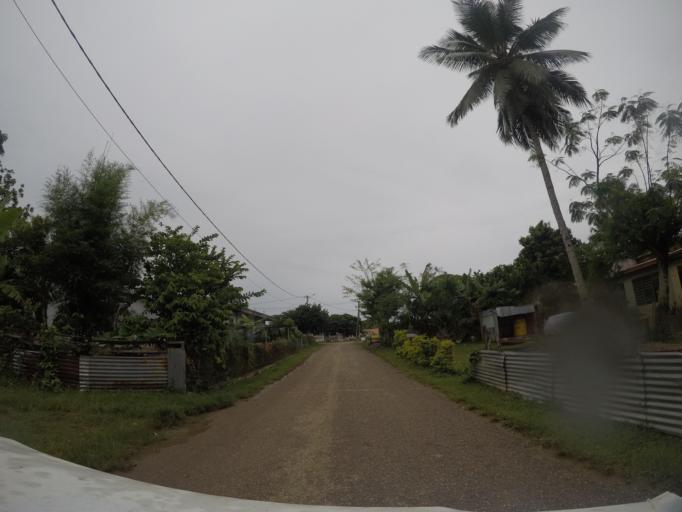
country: TL
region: Lautem
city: Lospalos
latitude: -8.5222
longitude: 126.9996
